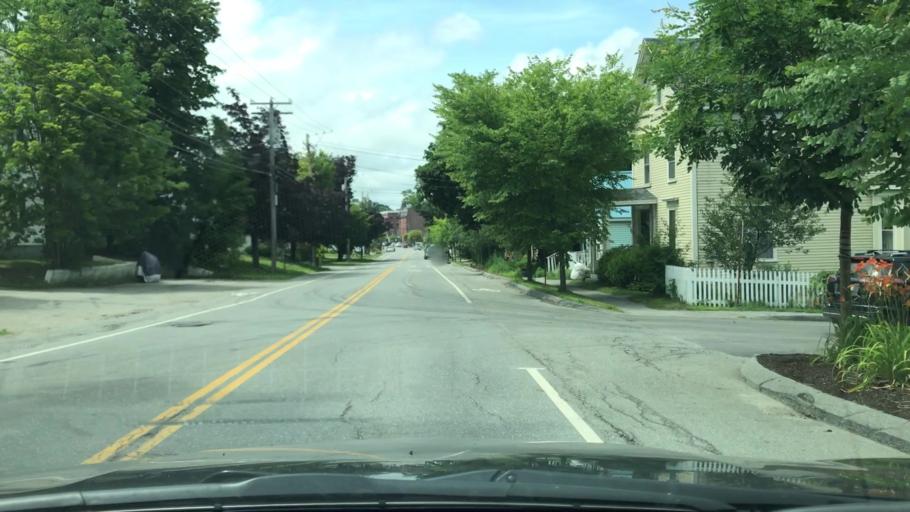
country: US
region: Maine
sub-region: Waldo County
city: Belfast
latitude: 44.4241
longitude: -69.0026
